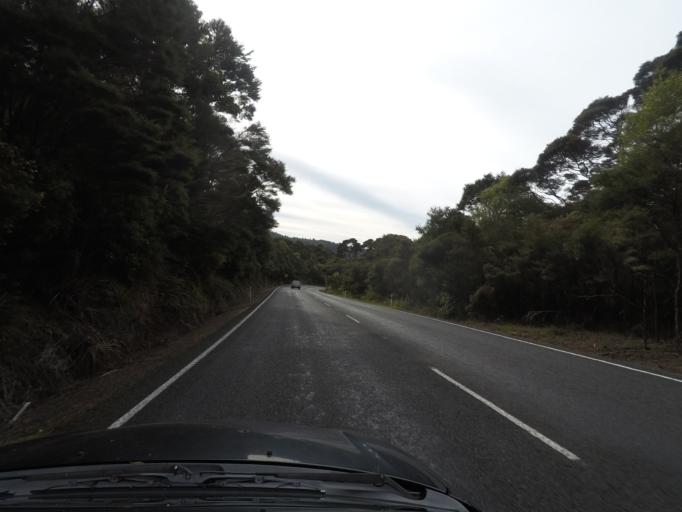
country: NZ
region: Auckland
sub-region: Auckland
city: Titirangi
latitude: -36.9393
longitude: 174.5547
